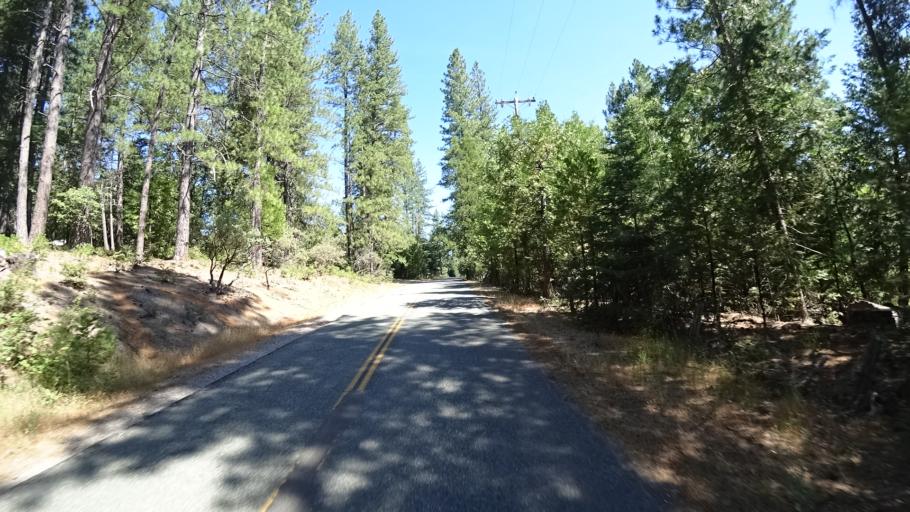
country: US
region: California
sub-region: Amador County
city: Pioneer
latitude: 38.4066
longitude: -120.5058
